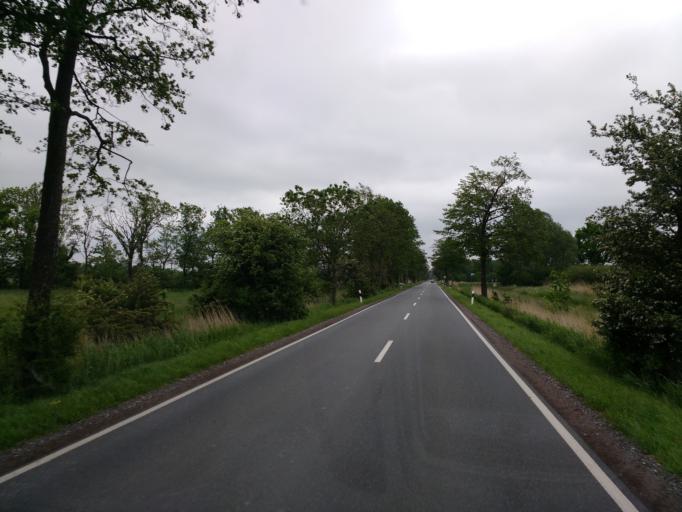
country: DE
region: Lower Saxony
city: Sillenstede
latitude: 53.6107
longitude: 7.9418
